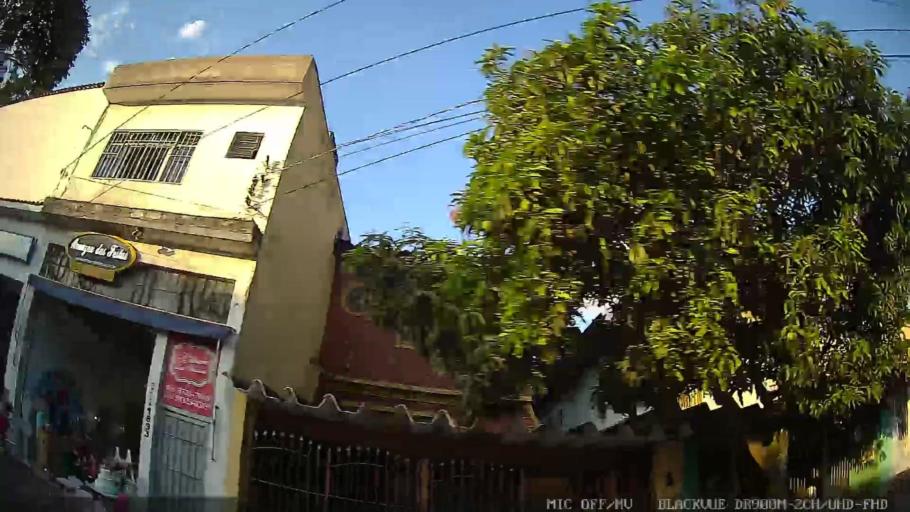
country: BR
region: Sao Paulo
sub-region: Sao Caetano Do Sul
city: Sao Caetano do Sul
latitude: -23.5845
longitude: -46.5403
